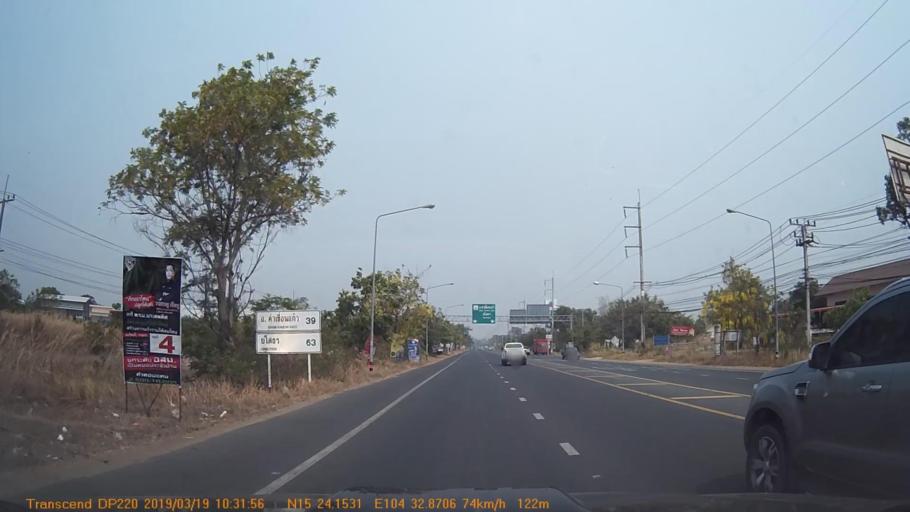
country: TH
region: Changwat Ubon Ratchathani
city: Khueang Nai
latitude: 15.4028
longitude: 104.5478
